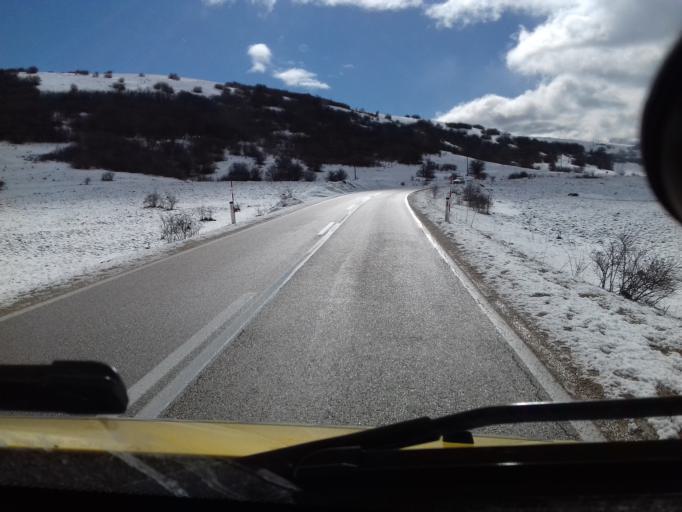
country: BA
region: Federation of Bosnia and Herzegovina
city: Tomislavgrad
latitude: 43.8130
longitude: 17.2025
